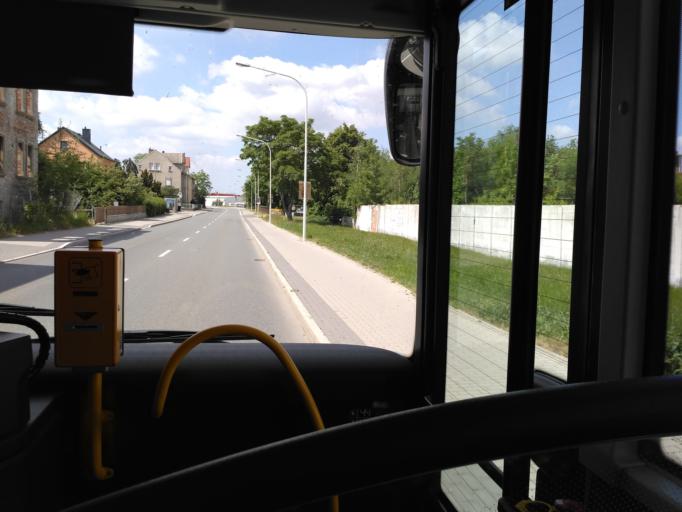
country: DE
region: Saxony
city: Riesa
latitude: 51.3251
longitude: 13.2761
